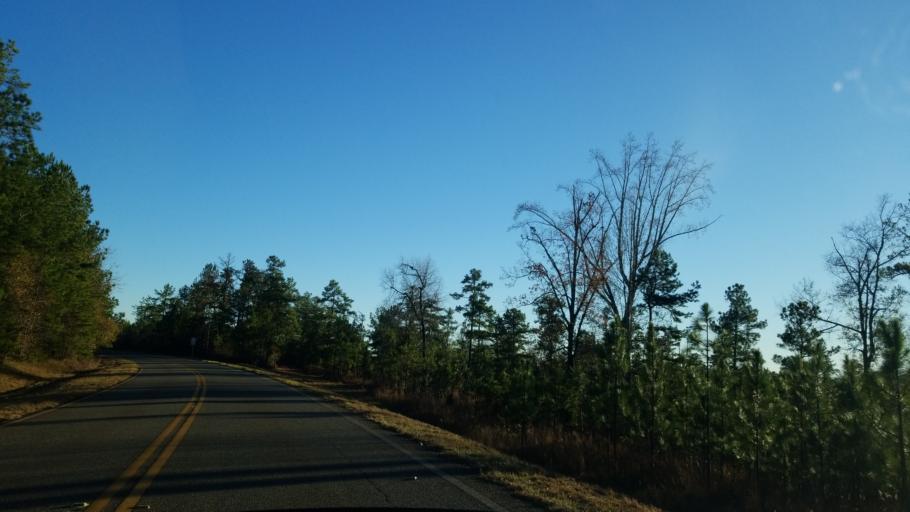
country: US
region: Georgia
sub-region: Chattahoochee County
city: Cusseta
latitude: 32.3282
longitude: -84.6590
